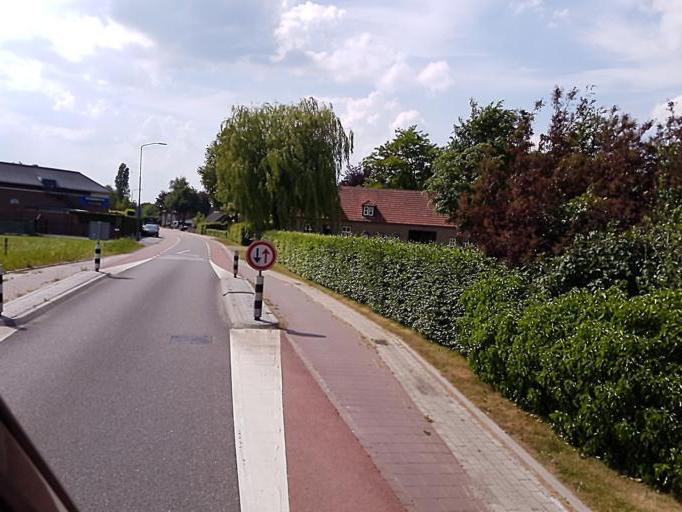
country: NL
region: North Brabant
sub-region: Gemeente Cranendonck
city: Cranendonck
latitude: 51.2628
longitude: 5.5815
